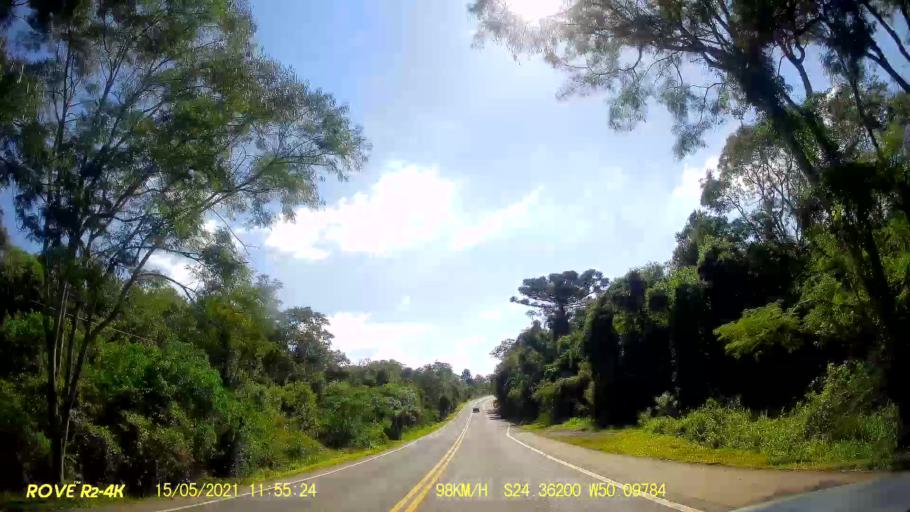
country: BR
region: Parana
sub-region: Pirai Do Sul
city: Pirai do Sul
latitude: -24.3620
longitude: -50.0978
